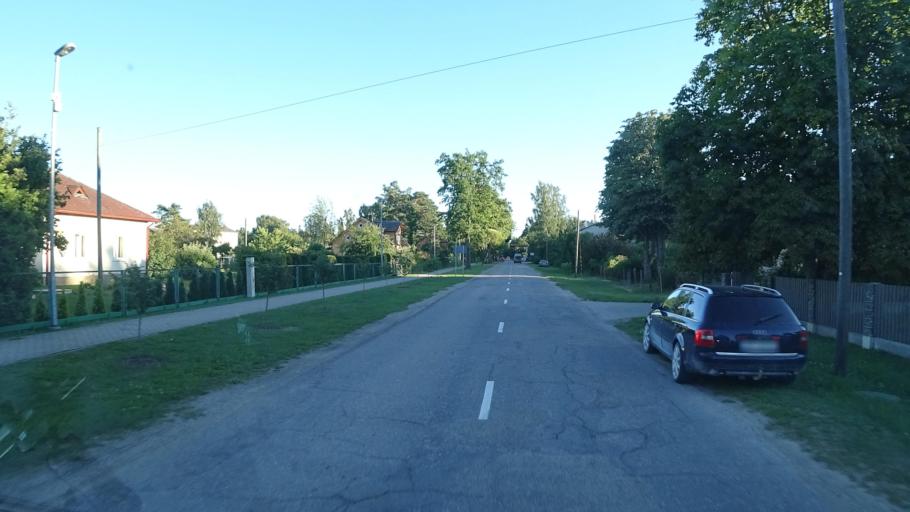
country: LV
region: Dundaga
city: Dundaga
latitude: 57.7402
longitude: 22.5831
